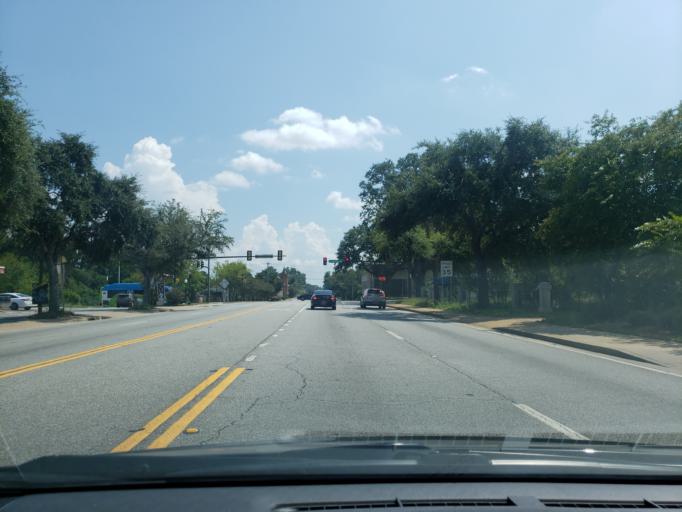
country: US
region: Georgia
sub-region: Dougherty County
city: Albany
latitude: 31.5745
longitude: -84.1560
